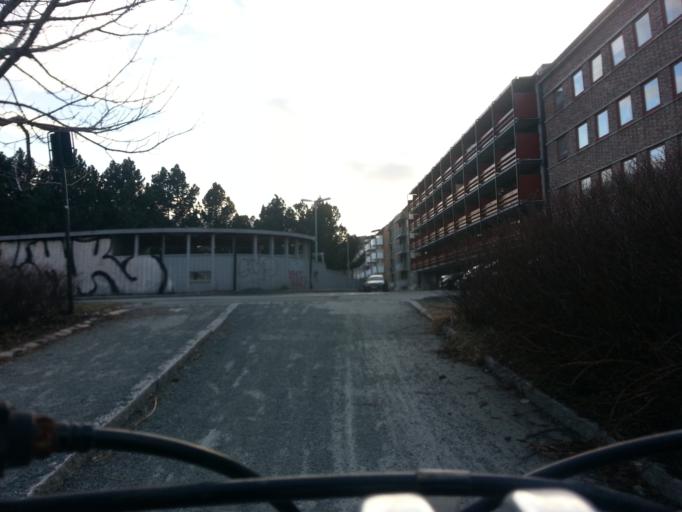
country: NO
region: Sor-Trondelag
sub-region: Trondheim
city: Trondheim
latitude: 63.4359
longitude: 10.4238
